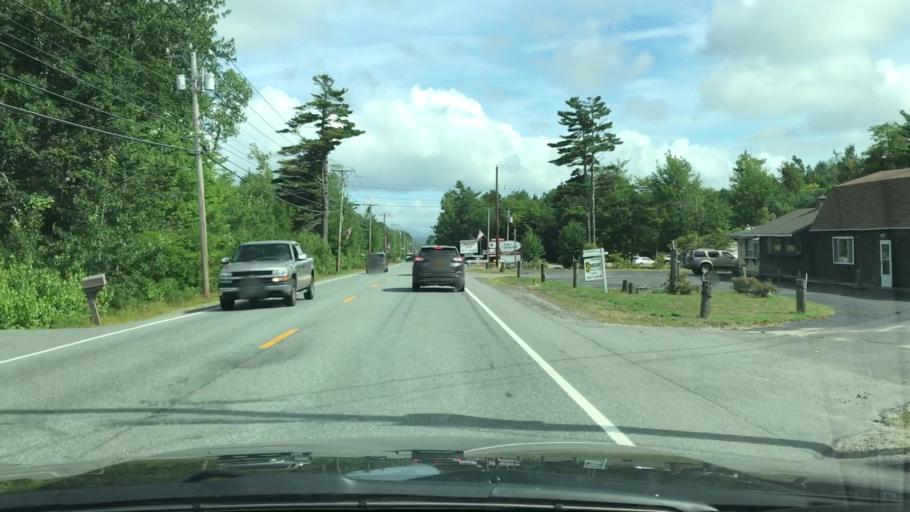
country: US
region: Maine
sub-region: Hancock County
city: Ellsworth
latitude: 44.5084
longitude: -68.3897
